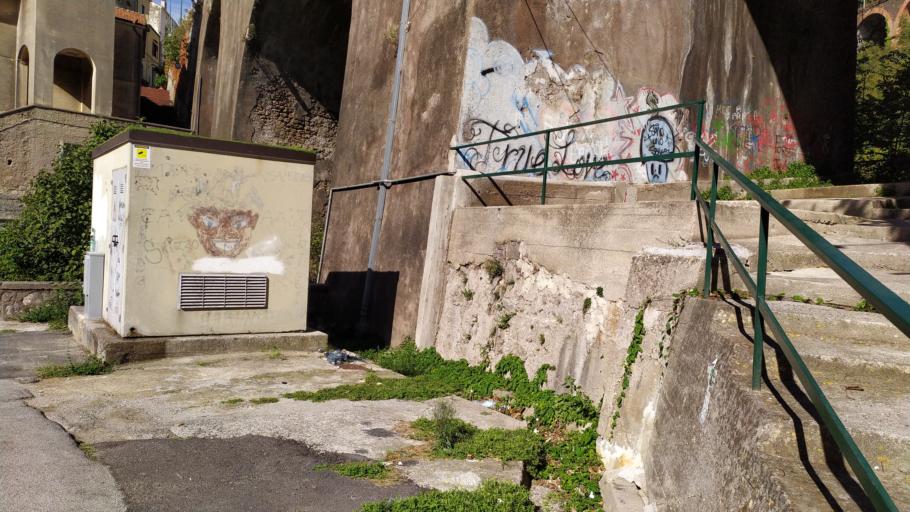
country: IT
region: Campania
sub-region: Provincia di Salerno
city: Dragonea
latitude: 40.6807
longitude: 14.7218
